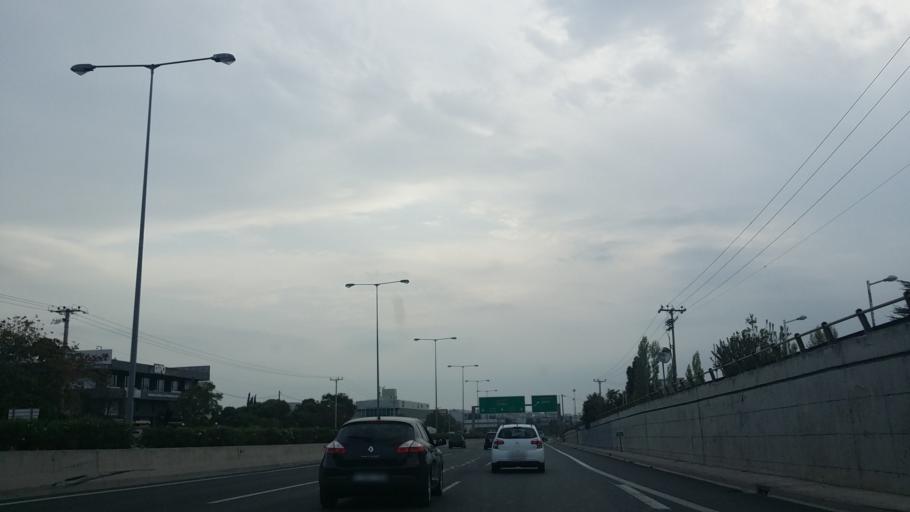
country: GR
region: Attica
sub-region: Nomarchia Athinas
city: Lykovrysi
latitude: 38.0832
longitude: 23.7846
